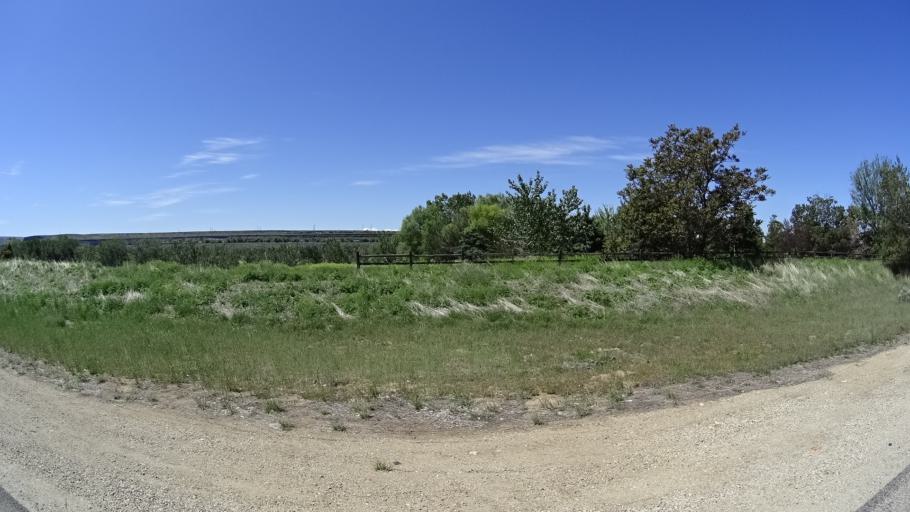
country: US
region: Idaho
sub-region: Ada County
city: Boise
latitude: 43.5600
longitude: -116.1025
